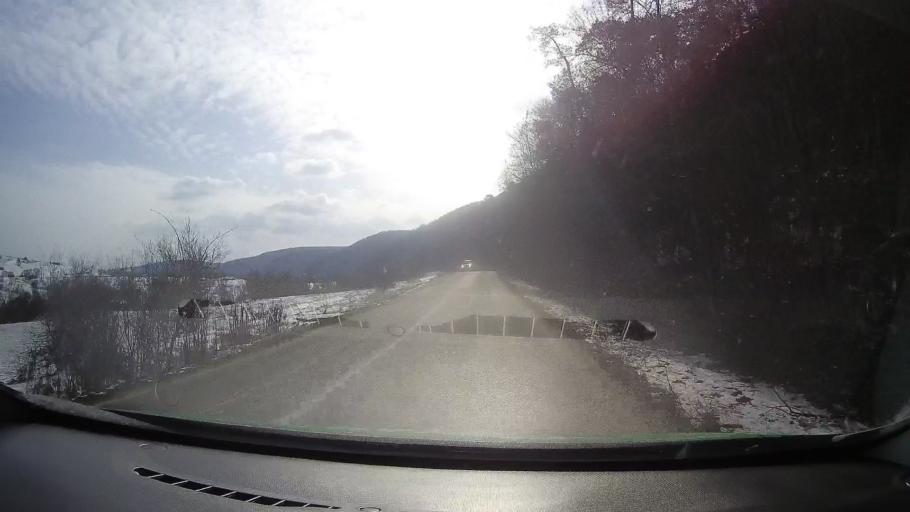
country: RO
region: Mures
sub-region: Comuna Apold
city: Saes
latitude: 46.1847
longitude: 24.7616
